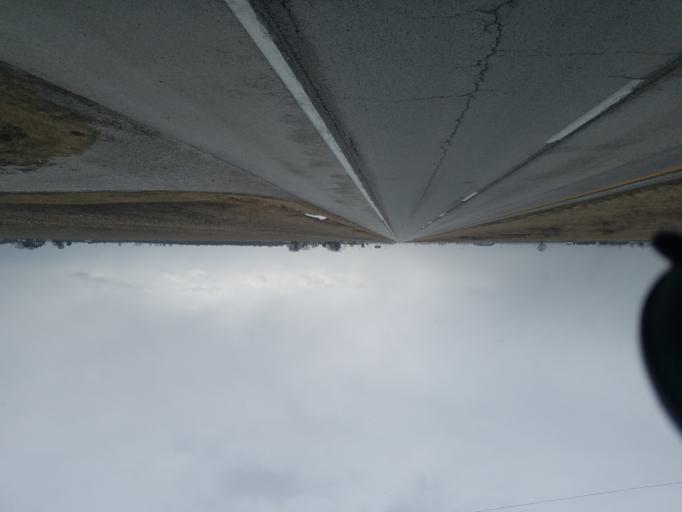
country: US
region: Missouri
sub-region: Randolph County
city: Huntsville
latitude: 39.5695
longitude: -92.4639
